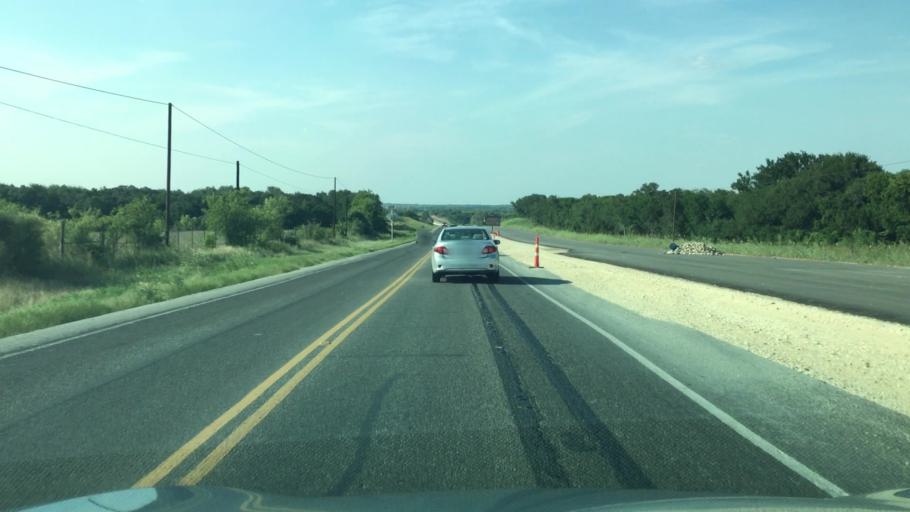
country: US
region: Texas
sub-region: Hays County
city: Buda
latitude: 30.0535
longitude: -97.8744
